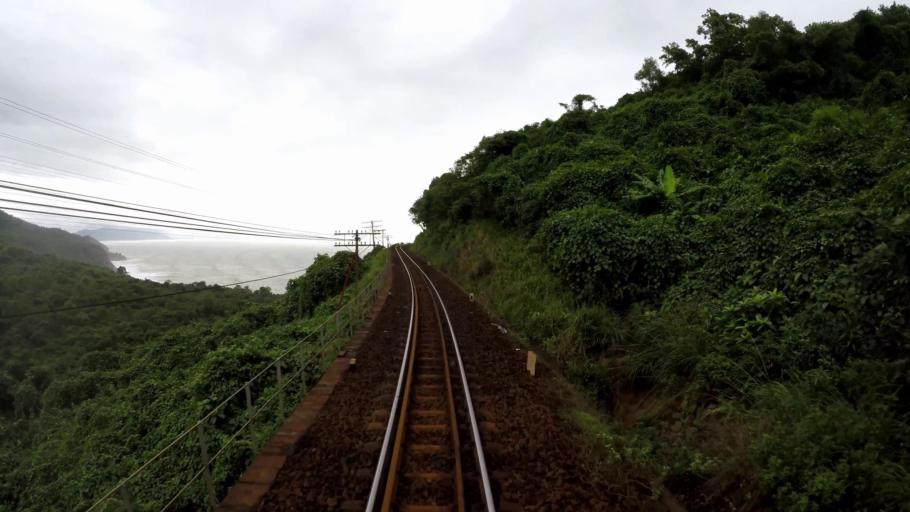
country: VN
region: Da Nang
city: Lien Chieu
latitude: 16.2082
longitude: 108.1229
